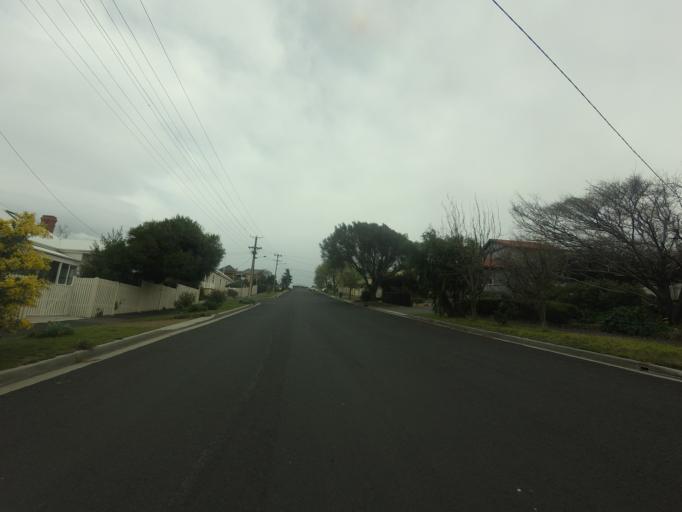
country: AU
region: Tasmania
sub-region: Clarence
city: Bellerive
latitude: -42.8776
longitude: 147.3685
